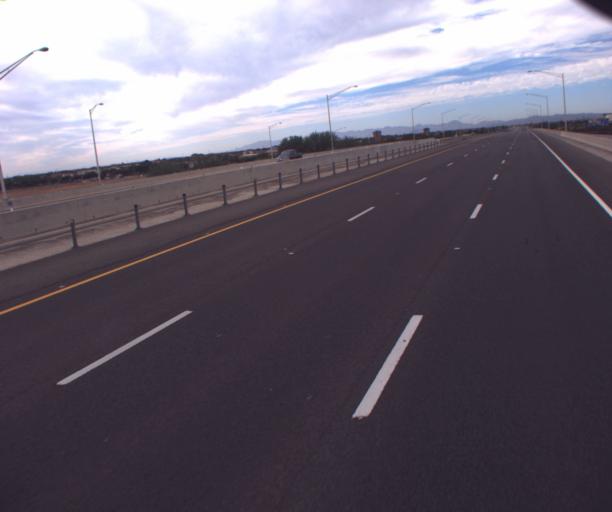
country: US
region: Arizona
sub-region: Maricopa County
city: Queen Creek
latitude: 33.3285
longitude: -111.6821
